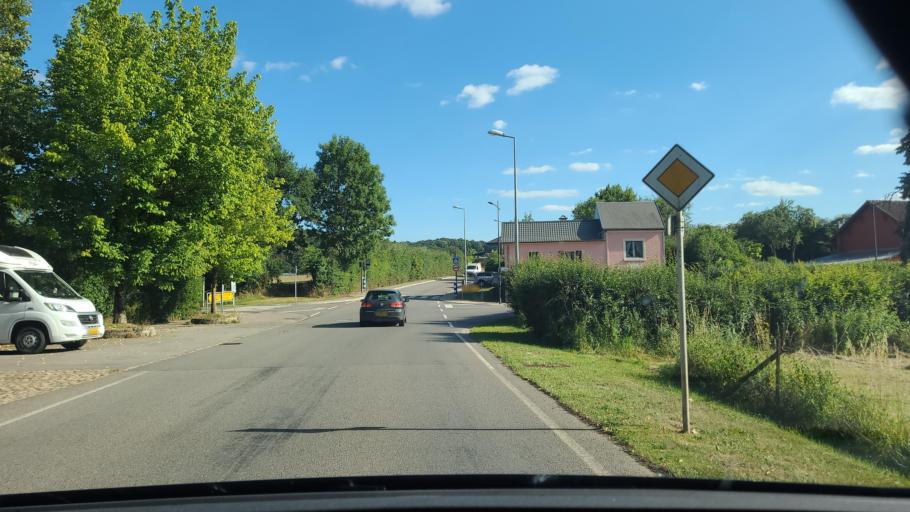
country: LU
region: Luxembourg
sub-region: Canton de Capellen
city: Dippach
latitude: 49.6137
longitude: 5.9903
